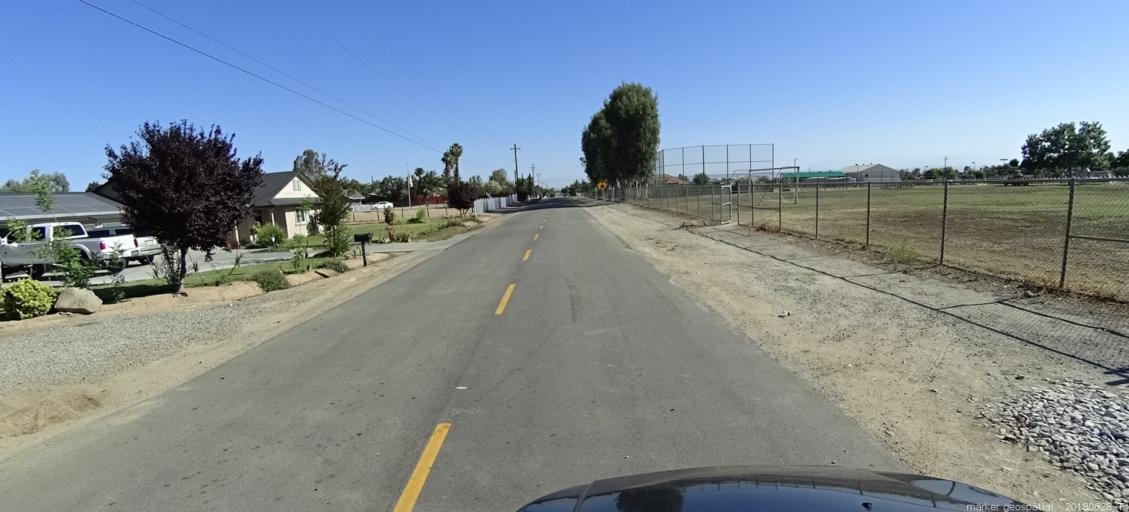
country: US
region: California
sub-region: Madera County
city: Bonadelle Ranchos-Madera Ranchos
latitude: 36.9866
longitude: -119.8829
